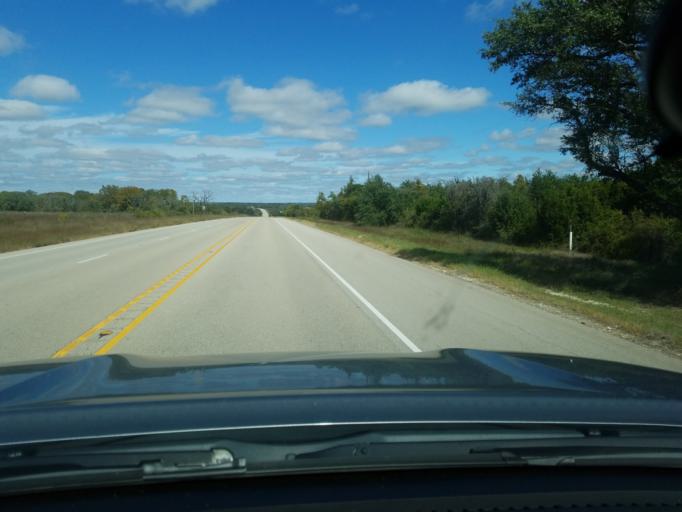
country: US
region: Texas
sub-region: Hamilton County
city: Hamilton
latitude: 31.5727
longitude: -98.1580
